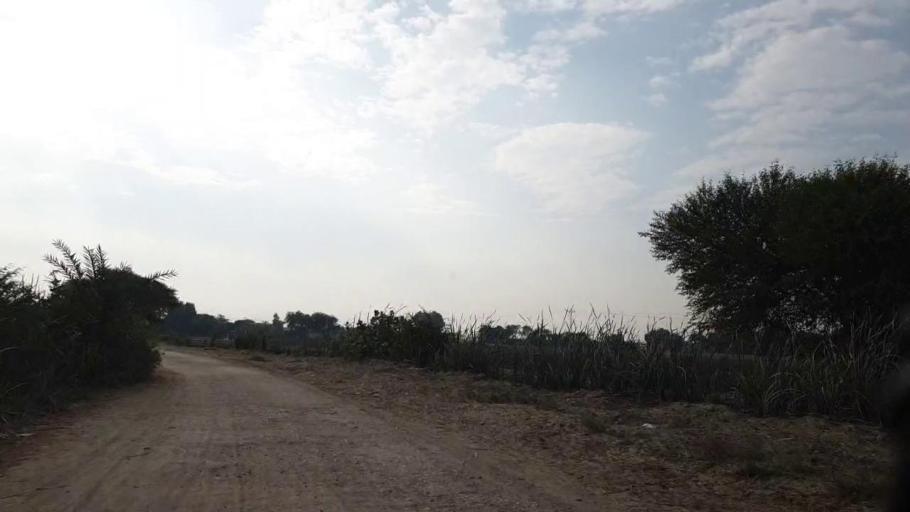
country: PK
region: Sindh
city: Tando Muhammad Khan
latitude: 25.0363
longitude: 68.4360
